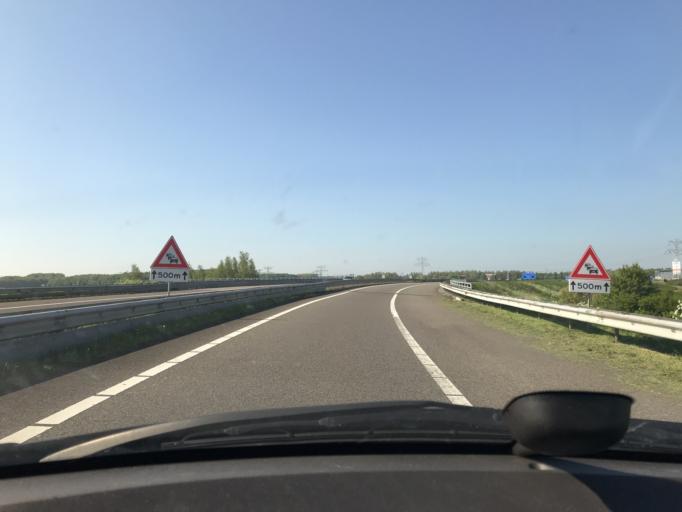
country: NL
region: Zeeland
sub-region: Gemeente Goes
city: Goes
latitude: 51.4817
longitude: 3.8700
